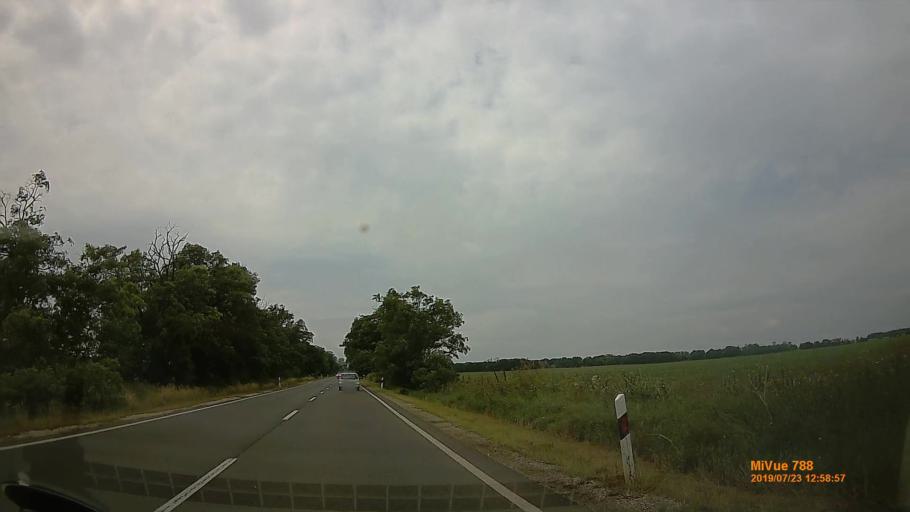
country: HU
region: Szabolcs-Szatmar-Bereg
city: Tiszalok
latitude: 47.9594
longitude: 21.4464
